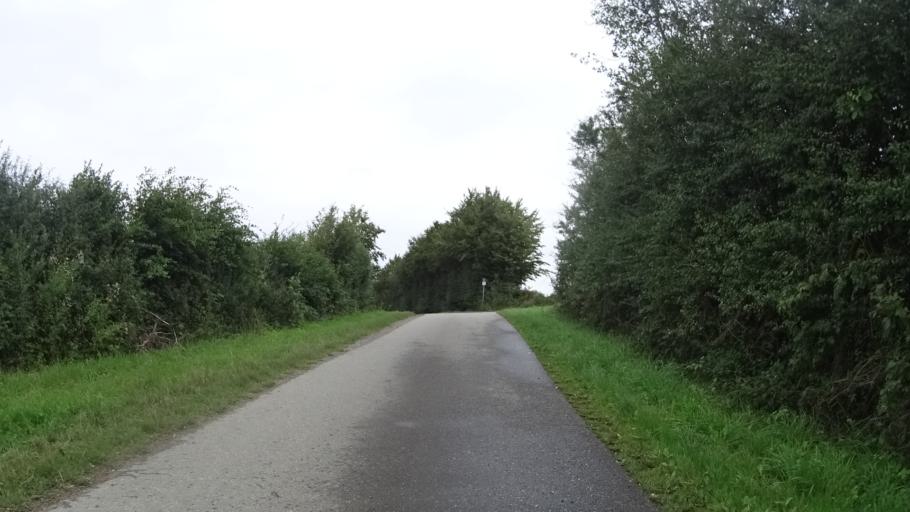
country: DE
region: Schleswig-Holstein
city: Klinkrade
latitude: 53.7123
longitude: 10.5437
